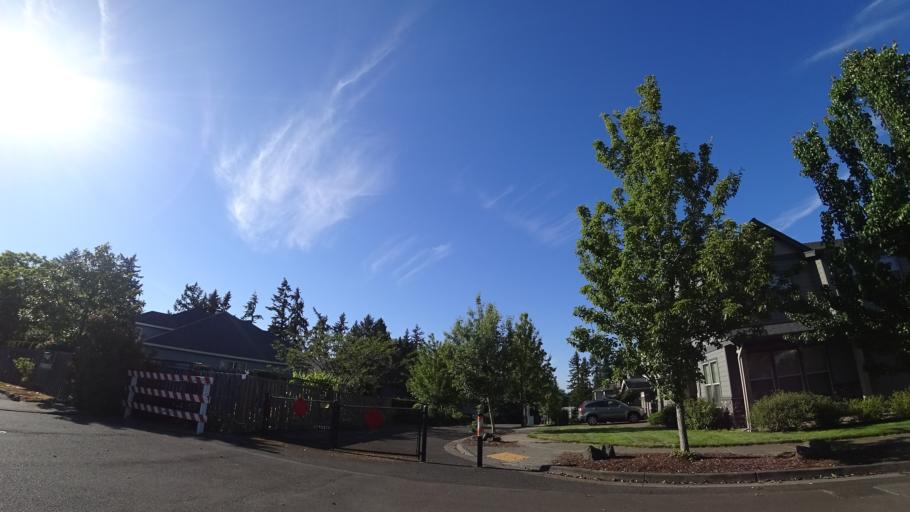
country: US
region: Oregon
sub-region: Washington County
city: Beaverton
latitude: 45.4635
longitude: -122.8150
